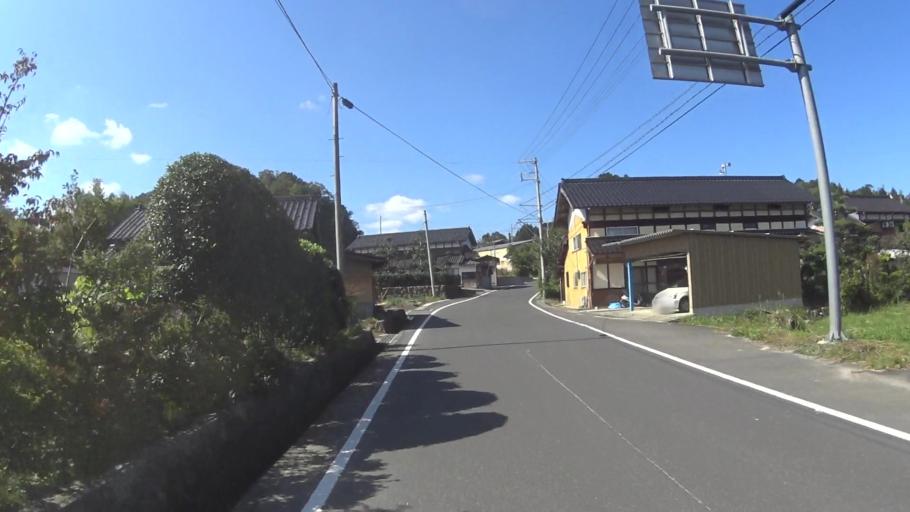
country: JP
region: Hyogo
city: Toyooka
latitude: 35.5931
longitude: 134.9557
